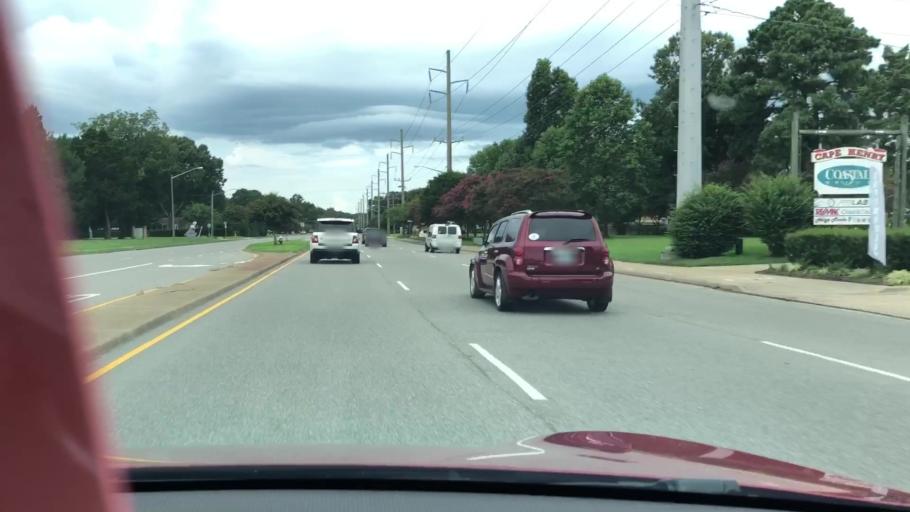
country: US
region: Virginia
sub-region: City of Virginia Beach
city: Virginia Beach
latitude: 36.8803
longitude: -76.0435
